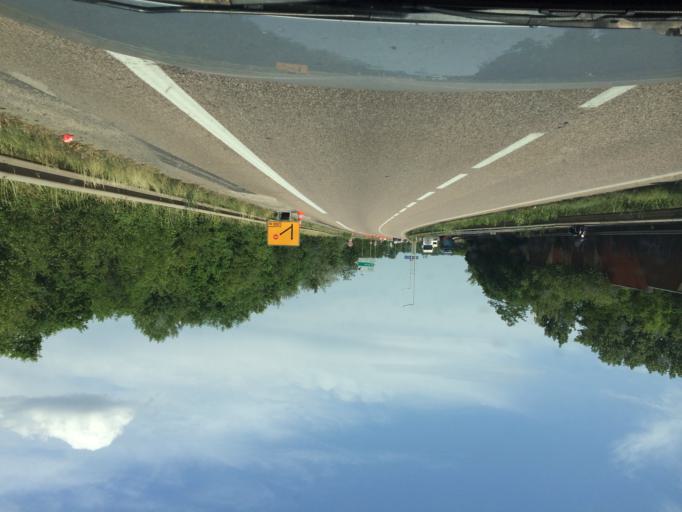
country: FR
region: Lorraine
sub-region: Departement de Meurthe-et-Moselle
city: Dommartin-les-Toul
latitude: 48.6717
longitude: 5.9190
